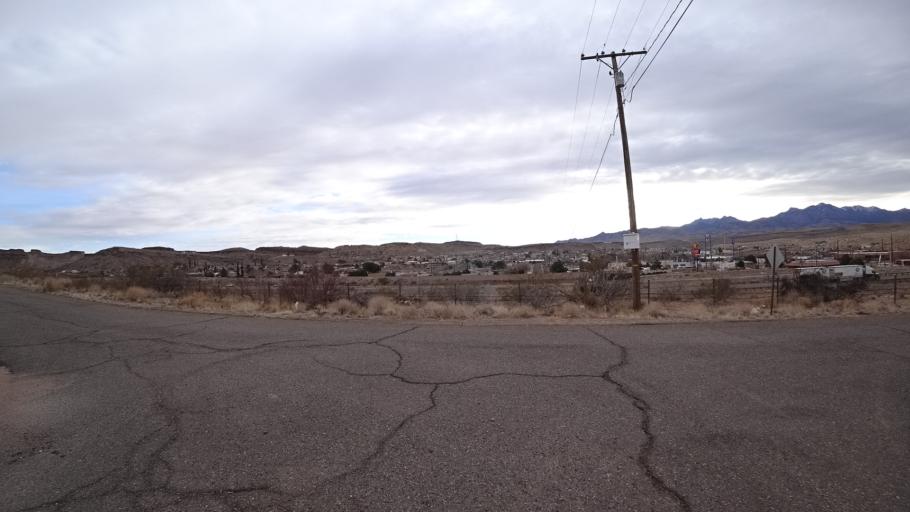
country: US
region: Arizona
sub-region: Mohave County
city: Kingman
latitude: 35.1946
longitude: -114.0685
